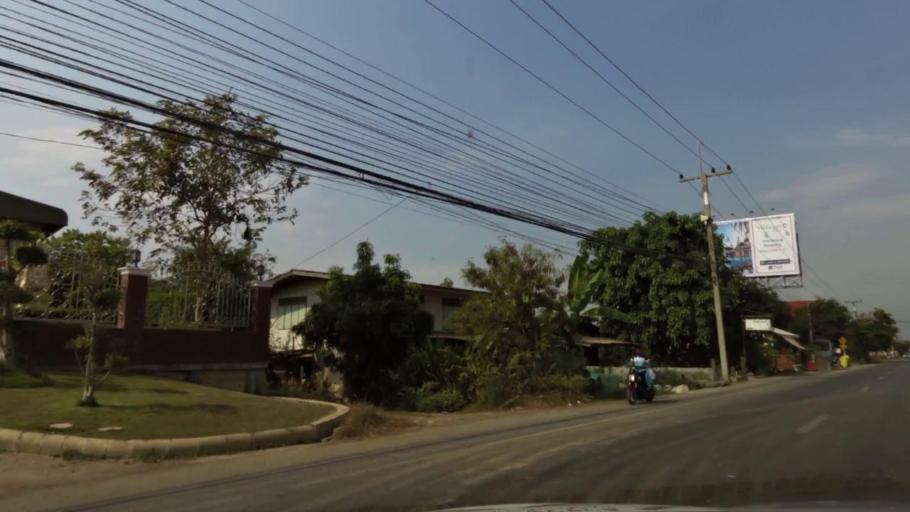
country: TH
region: Phra Nakhon Si Ayutthaya
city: Phra Nakhon Si Ayutthaya
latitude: 14.3255
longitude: 100.5757
